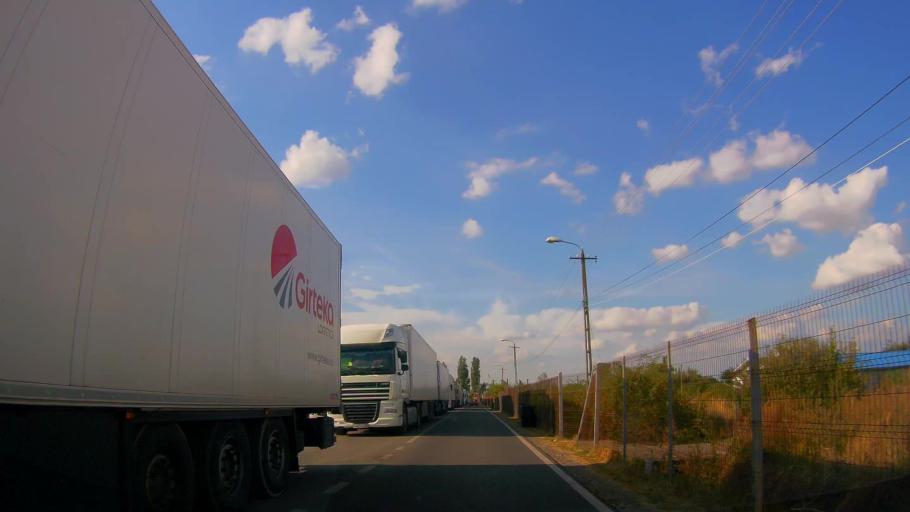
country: RO
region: Satu Mare
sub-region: Comuna Porumbesti
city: Porumbesti
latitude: 47.9942
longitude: 23.0024
